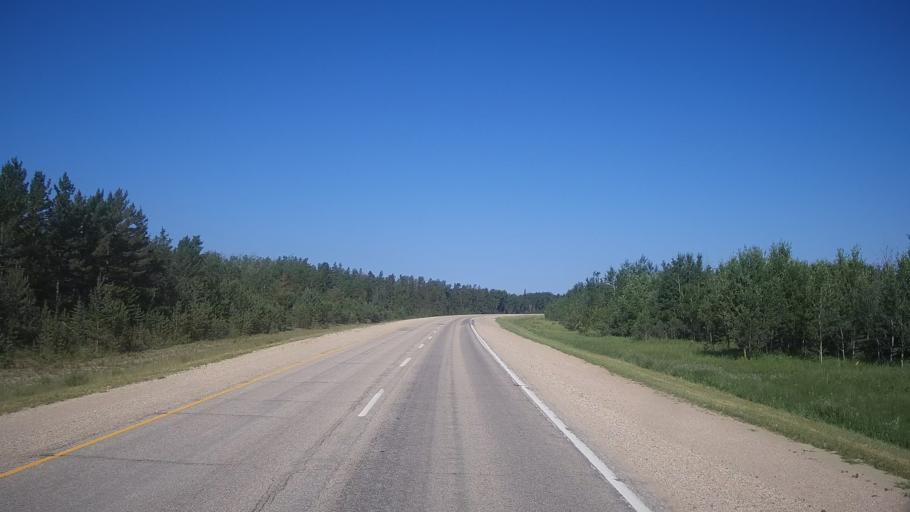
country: CA
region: Manitoba
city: La Broquerie
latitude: 49.6494
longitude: -95.9699
